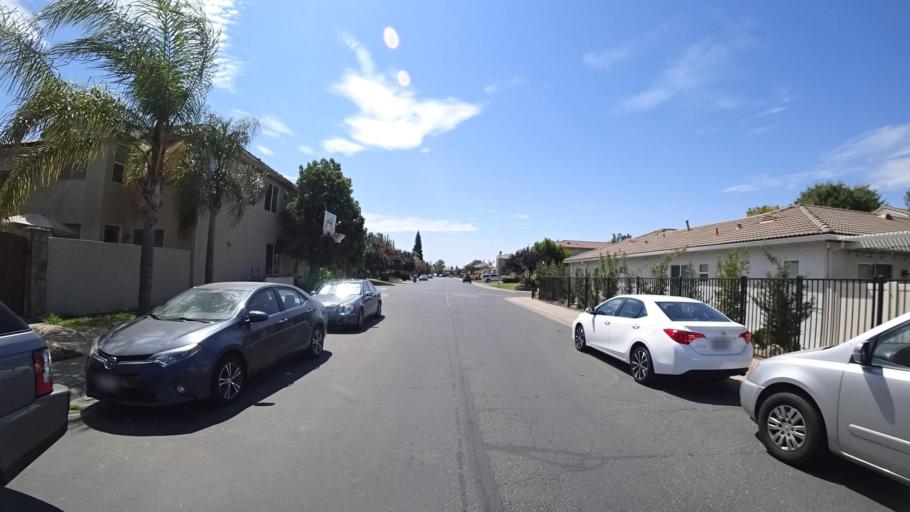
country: US
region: California
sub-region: Placer County
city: Rocklin
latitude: 38.8048
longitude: -121.2842
